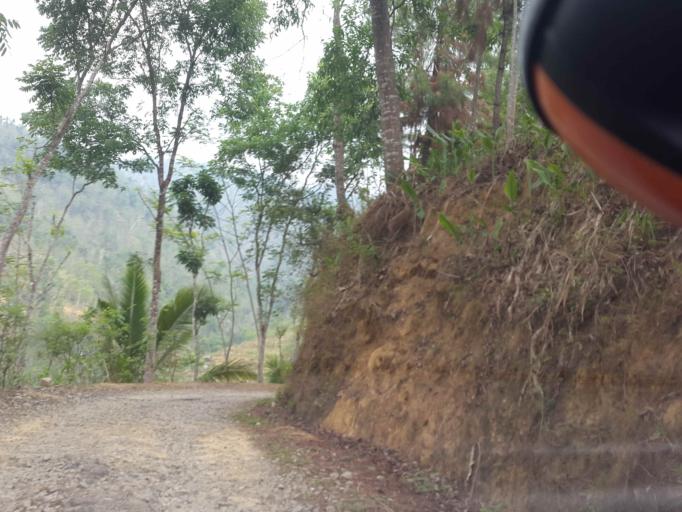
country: ID
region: East Java
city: Ploso
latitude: -8.0511
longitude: 111.1329
